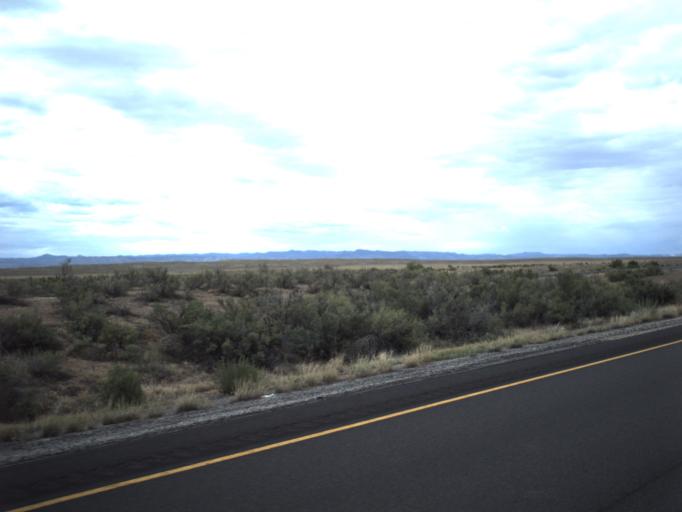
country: US
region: Colorado
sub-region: Mesa County
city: Loma
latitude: 39.0838
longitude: -109.2220
